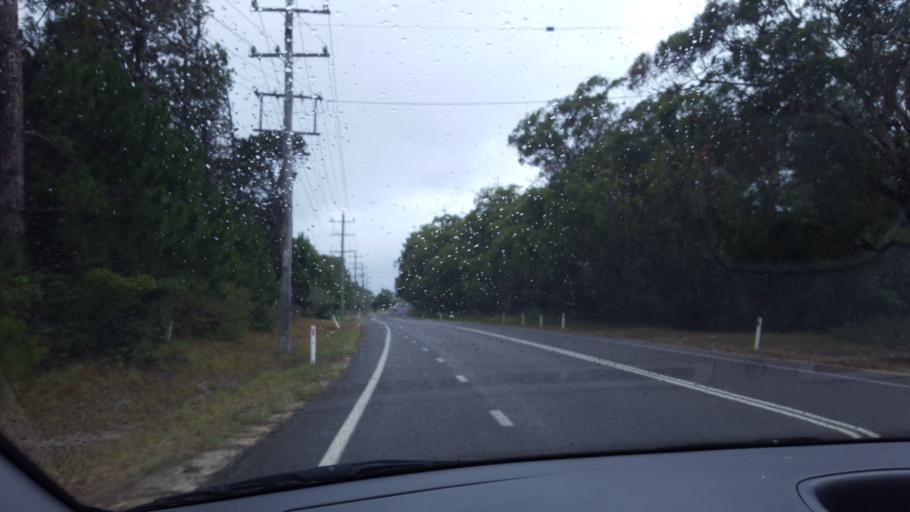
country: AU
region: New South Wales
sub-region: Port Stephens Shire
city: Anna Bay
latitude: -32.7703
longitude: 152.0748
